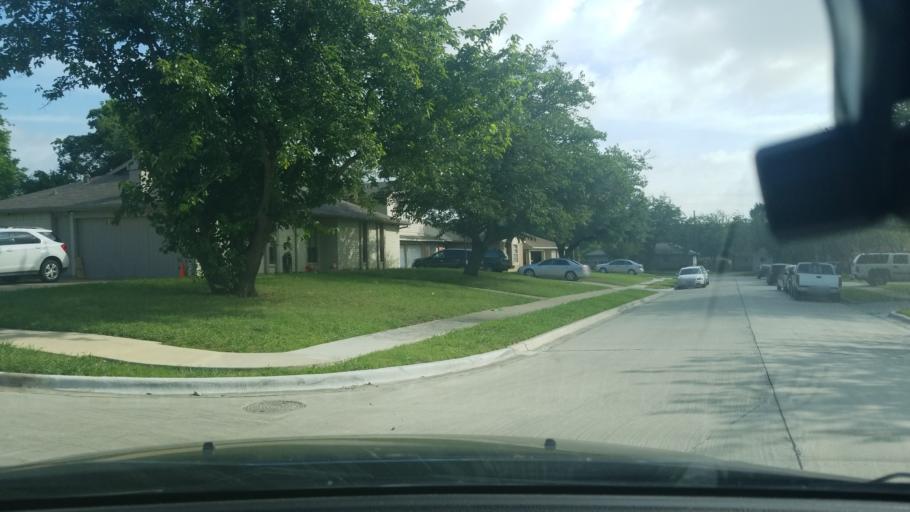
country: US
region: Texas
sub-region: Dallas County
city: Mesquite
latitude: 32.7731
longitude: -96.6370
